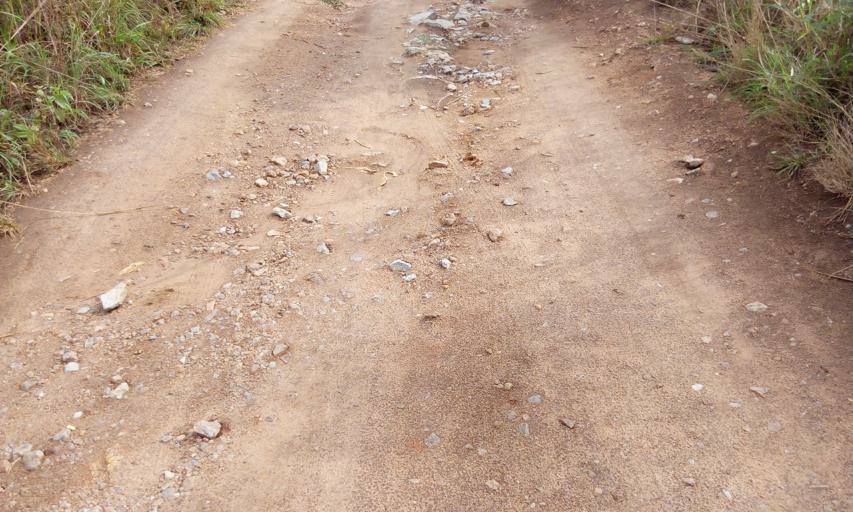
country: GH
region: Central
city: Winneba
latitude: 5.3623
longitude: -0.6208
